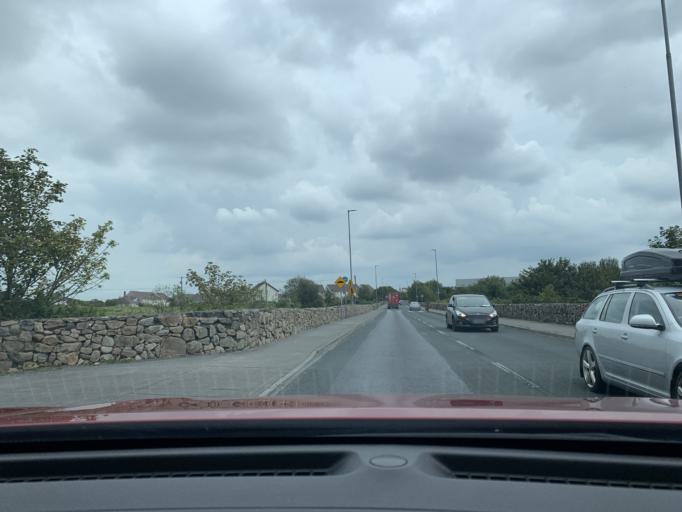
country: IE
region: Connaught
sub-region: County Galway
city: Gaillimh
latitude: 53.2772
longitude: -9.0969
